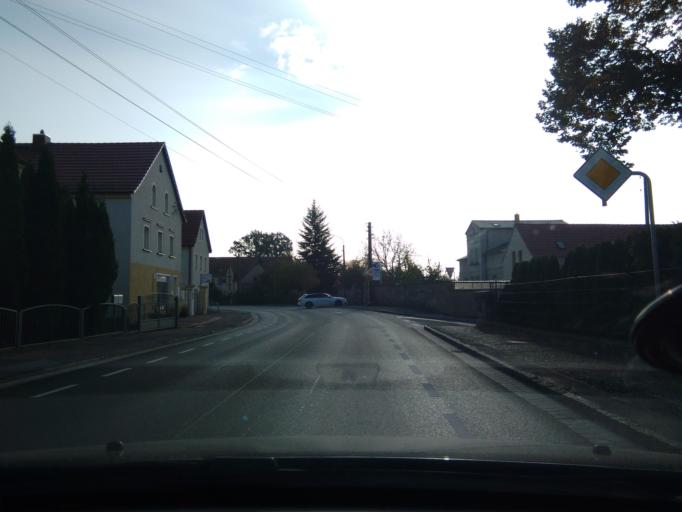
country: DE
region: Saxony
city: Coswig
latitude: 51.1298
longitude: 13.5457
